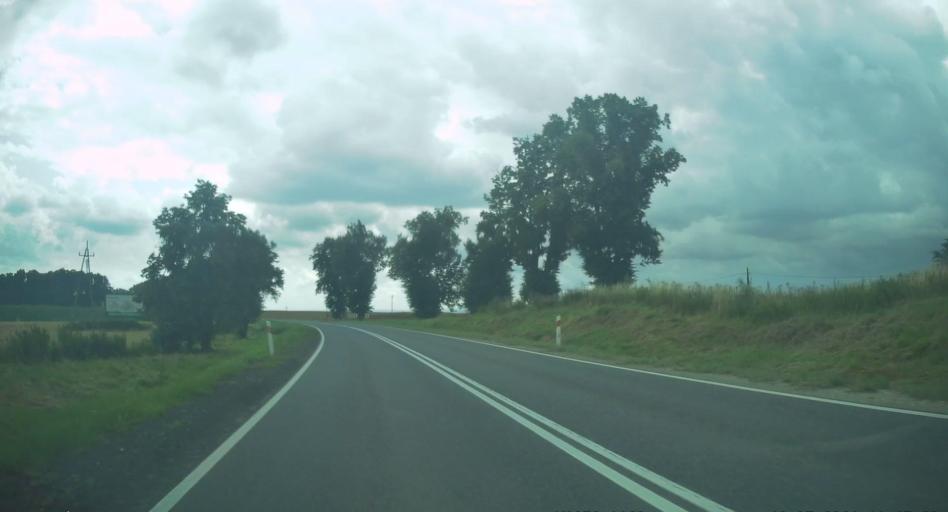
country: PL
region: Opole Voivodeship
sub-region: Powiat prudnicki
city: Laka Prudnicka
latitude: 50.3993
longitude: 17.5078
